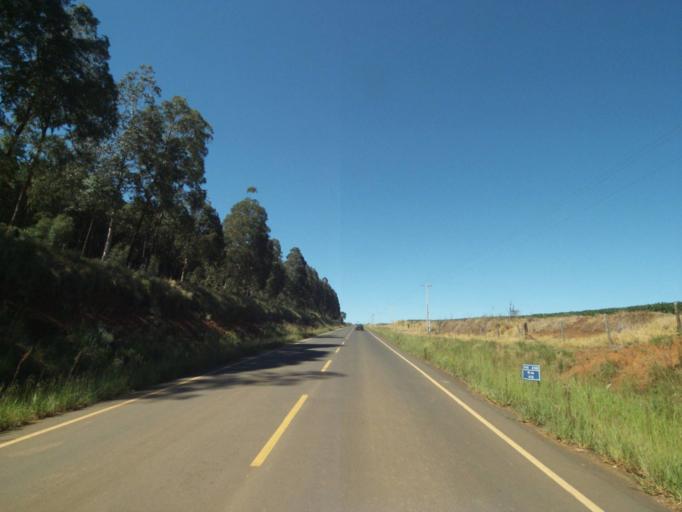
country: BR
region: Parana
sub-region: Pinhao
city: Pinhao
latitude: -25.8305
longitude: -52.0197
